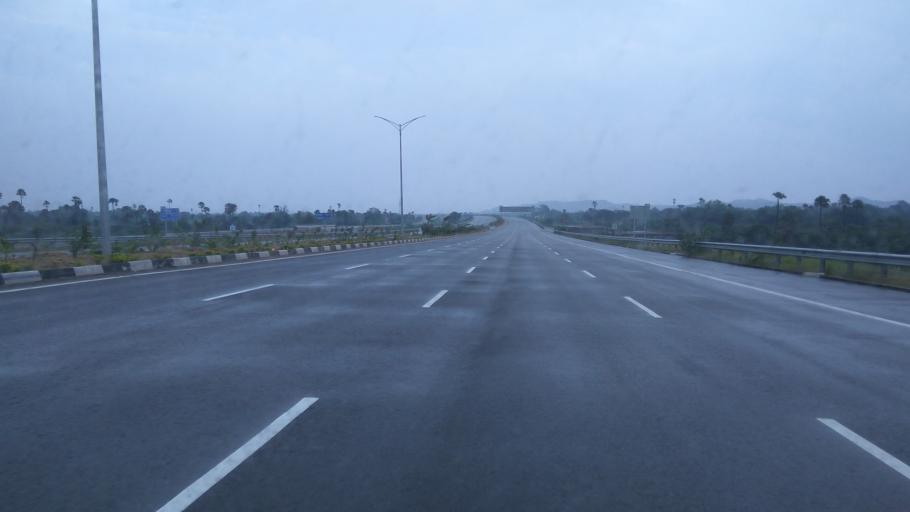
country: IN
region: Telangana
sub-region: Rangareddi
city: Ghatkesar
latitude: 17.4572
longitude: 78.6695
